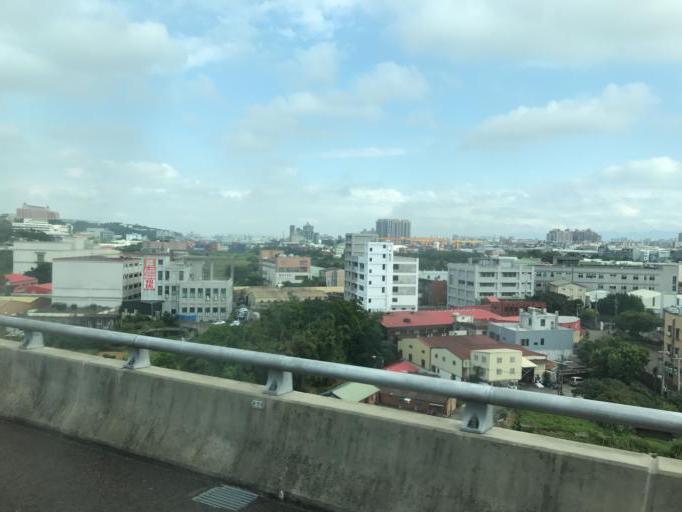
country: TW
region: Taiwan
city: Daxi
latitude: 24.9142
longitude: 121.1667
